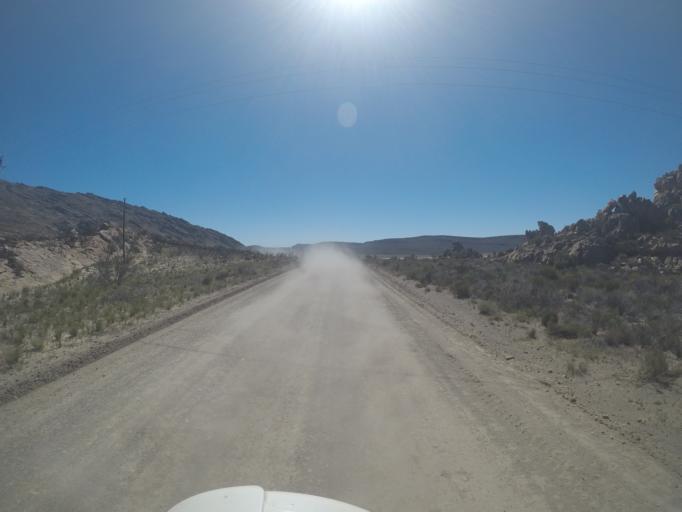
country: ZA
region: Western Cape
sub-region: Cape Winelands District Municipality
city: Ceres
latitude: -32.8528
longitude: 19.4451
